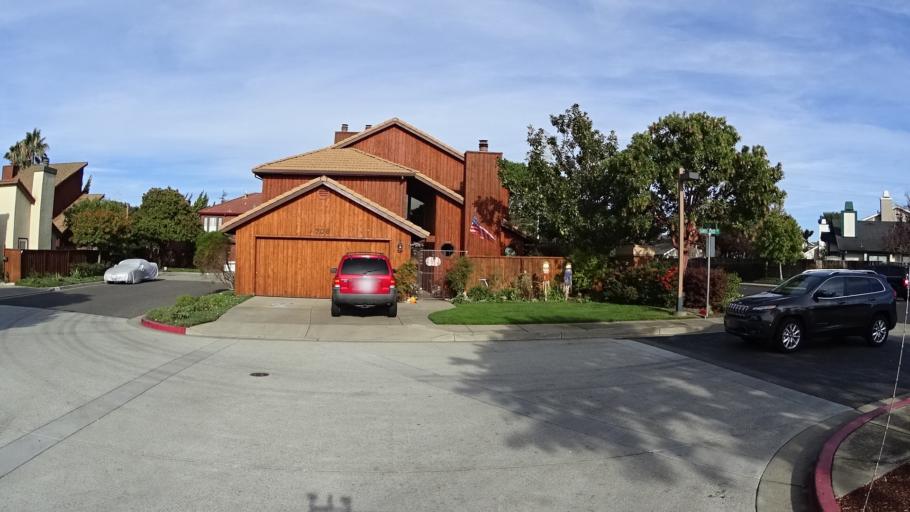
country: US
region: California
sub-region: San Mateo County
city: Redwood Shores
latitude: 37.5425
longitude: -122.2618
